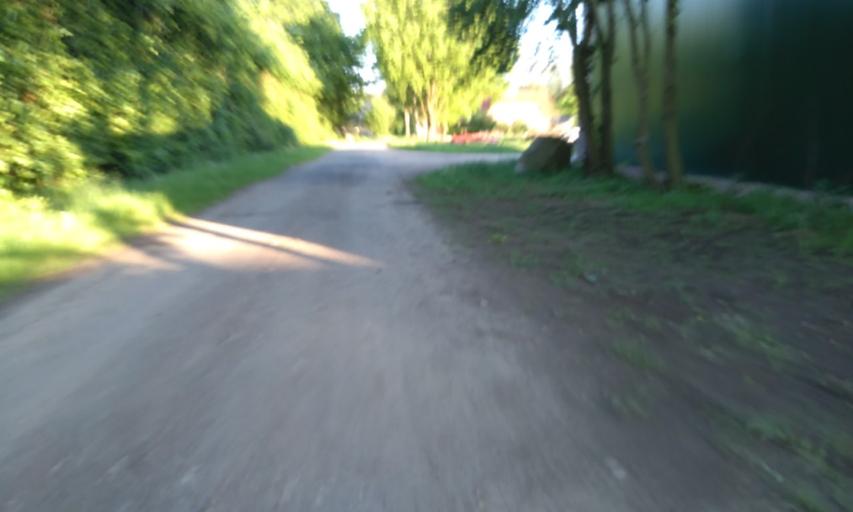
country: DE
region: Lower Saxony
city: Bliedersdorf
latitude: 53.4887
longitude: 9.5705
